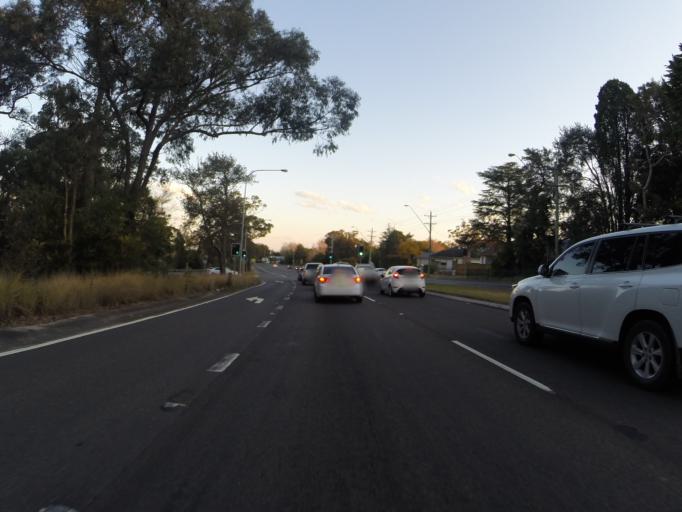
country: AU
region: New South Wales
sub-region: Blue Mountains Municipality
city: Blaxland
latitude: -33.7372
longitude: 150.6050
